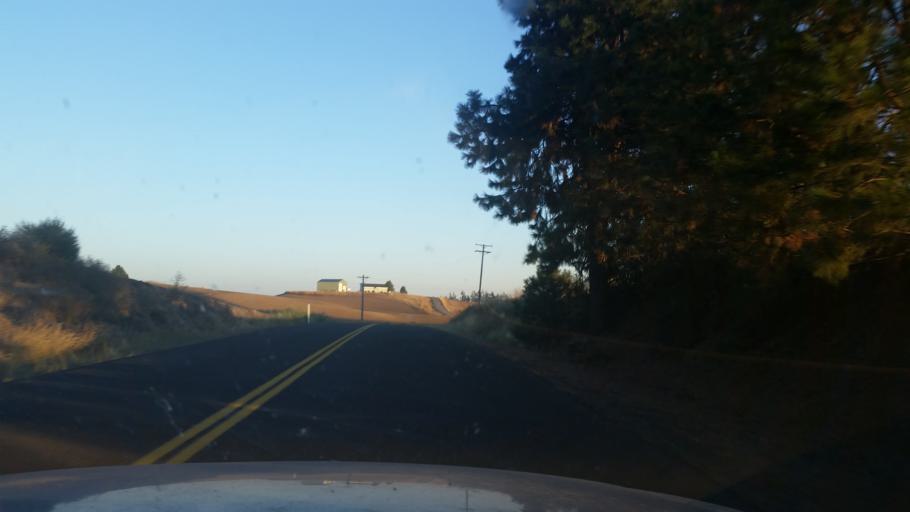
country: US
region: Washington
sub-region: Spokane County
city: Cheney
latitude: 47.5175
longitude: -117.5952
